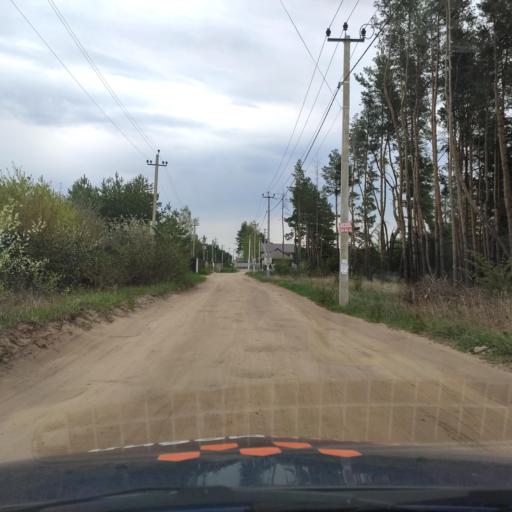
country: RU
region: Voronezj
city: Podgornoye
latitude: 51.8585
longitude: 39.1604
